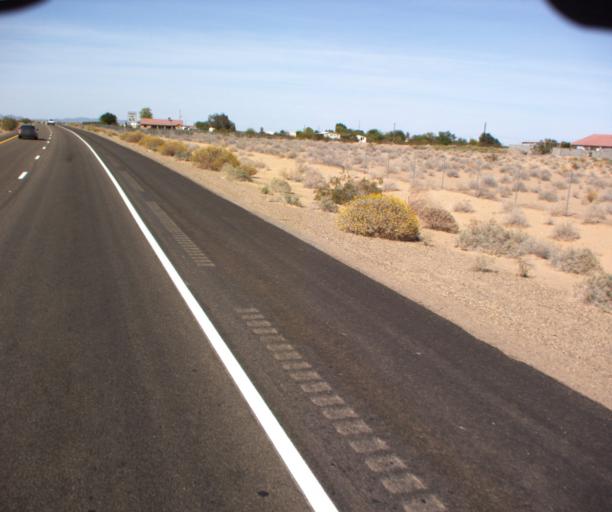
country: US
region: Arizona
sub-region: Yuma County
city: Fortuna Foothills
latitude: 32.6290
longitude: -114.5201
